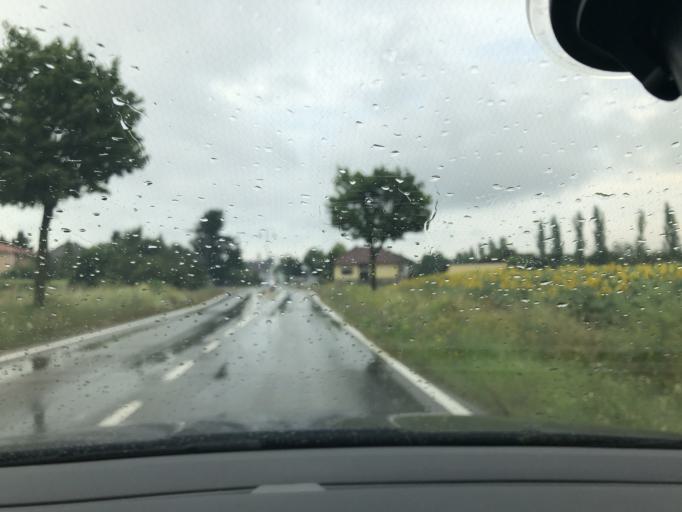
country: AT
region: Lower Austria
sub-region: Politischer Bezirk Ganserndorf
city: Gross-Schweinbarth
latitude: 48.4085
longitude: 16.6377
